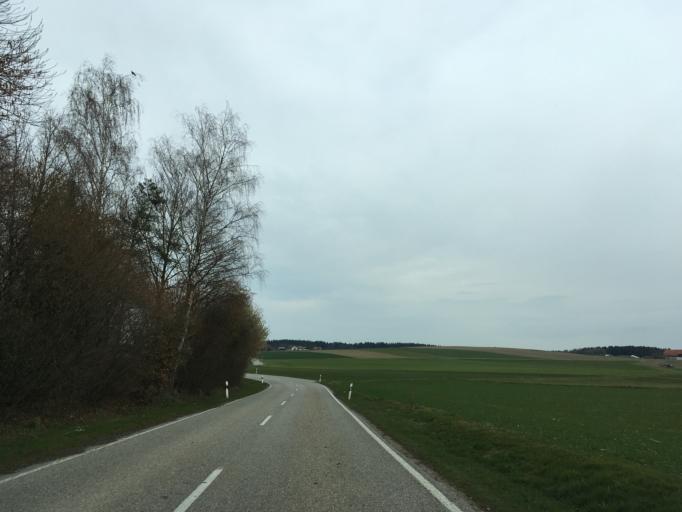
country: DE
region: Bavaria
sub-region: Upper Bavaria
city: Schnaitsee
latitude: 48.0457
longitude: 12.3748
